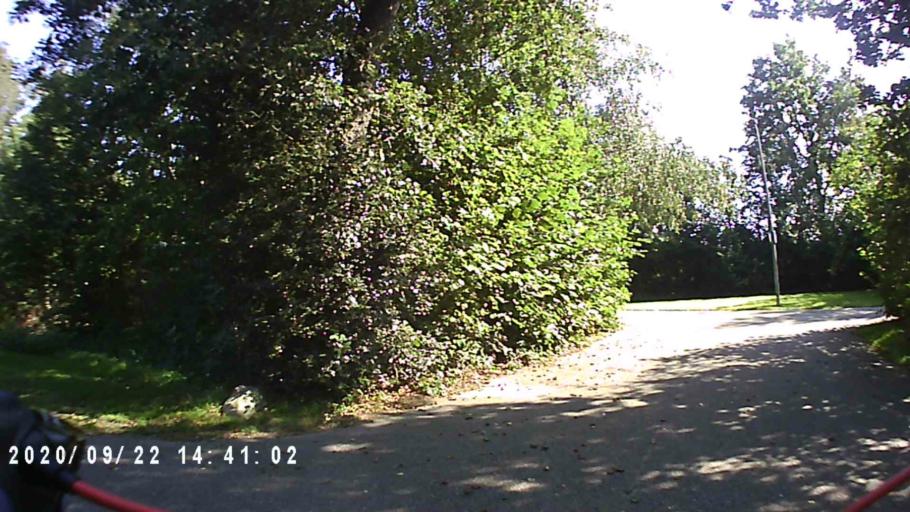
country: NL
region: Groningen
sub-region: Gemeente Leek
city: Leek
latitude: 53.0235
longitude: 6.3504
